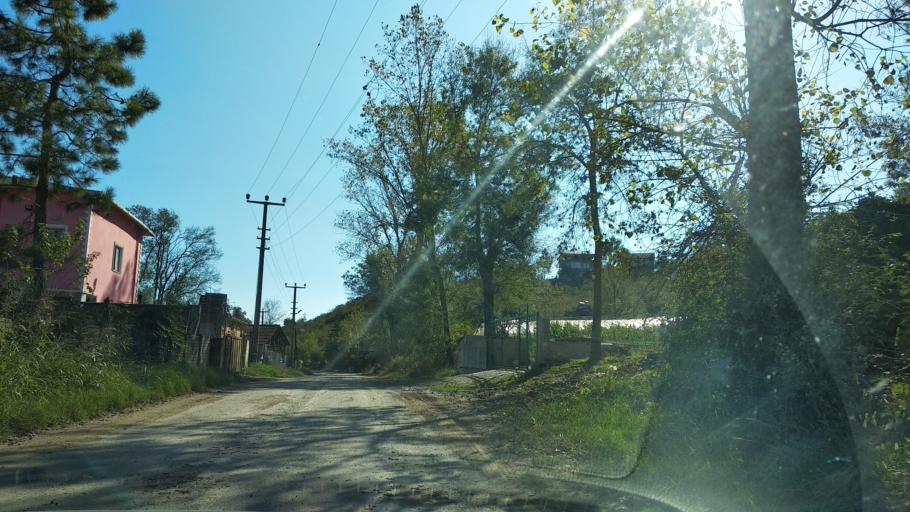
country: TR
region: Sakarya
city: Ortakoy
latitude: 41.0345
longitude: 30.5953
